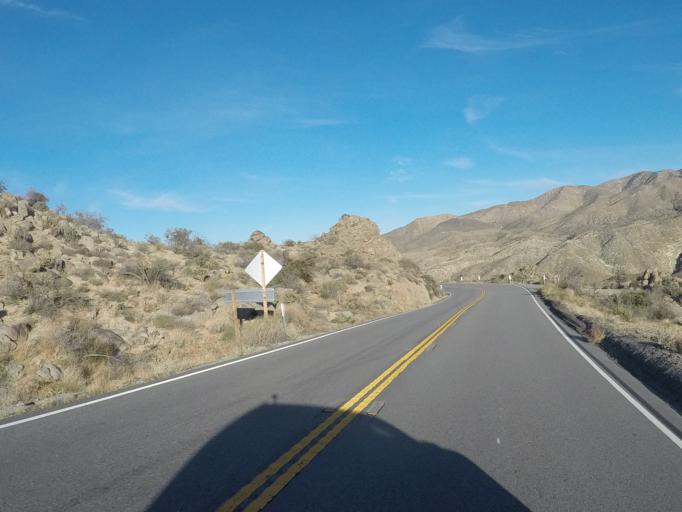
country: US
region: California
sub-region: Riverside County
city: Palm Desert
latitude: 33.6086
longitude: -116.4185
